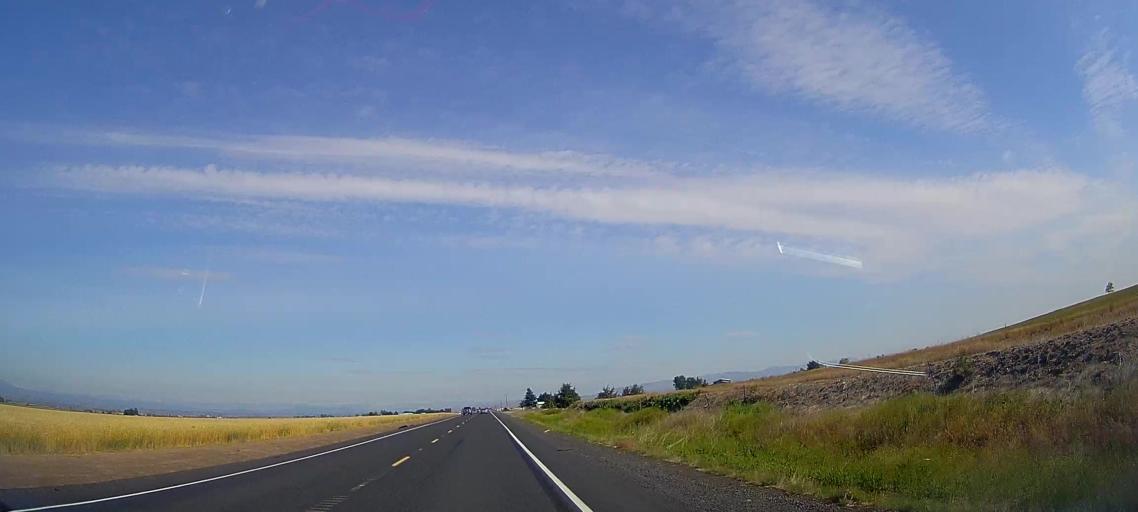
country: US
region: Oregon
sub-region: Jefferson County
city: Madras
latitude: 44.6723
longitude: -121.1414
